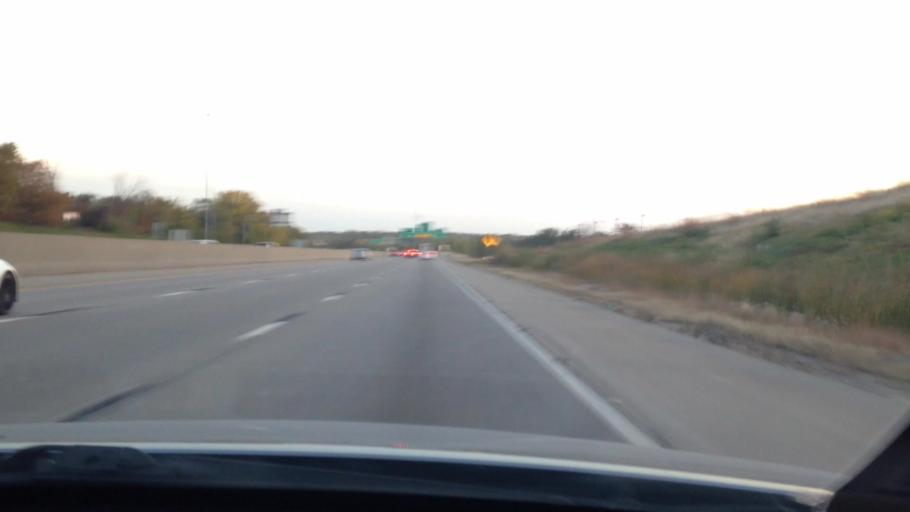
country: US
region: Kansas
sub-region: Johnson County
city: Merriam
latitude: 39.0528
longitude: -94.6794
